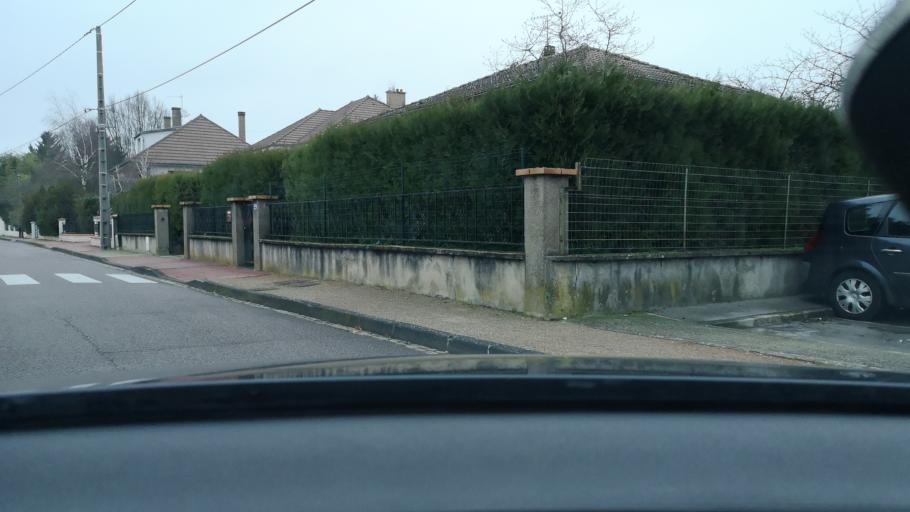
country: FR
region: Bourgogne
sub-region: Departement de Saone-et-Loire
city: Chalon-sur-Saone
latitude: 46.8048
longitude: 4.8513
